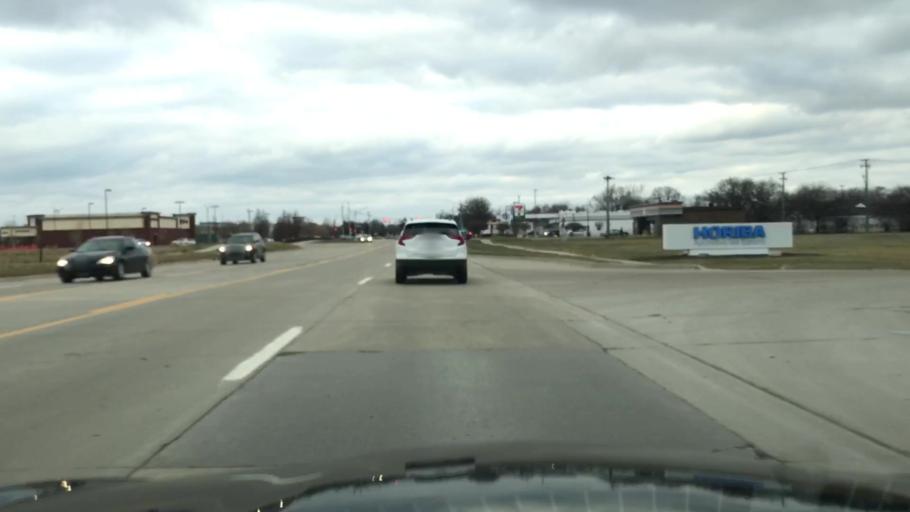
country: US
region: Michigan
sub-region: Oakland County
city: Clawson
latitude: 42.5579
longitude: -83.1079
